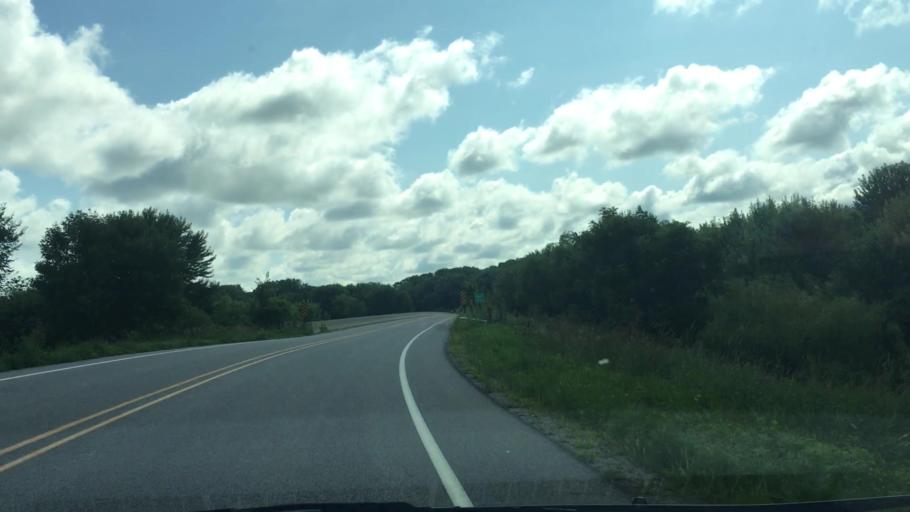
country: US
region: Iowa
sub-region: Linn County
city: Lisbon
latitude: 41.8452
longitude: -91.3931
